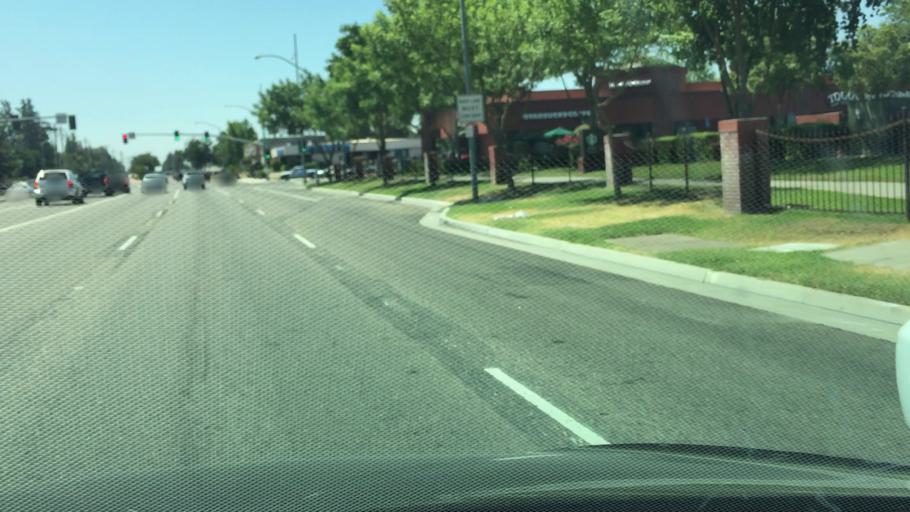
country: US
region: California
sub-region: Fresno County
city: Fresno
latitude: 36.8373
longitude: -119.8463
